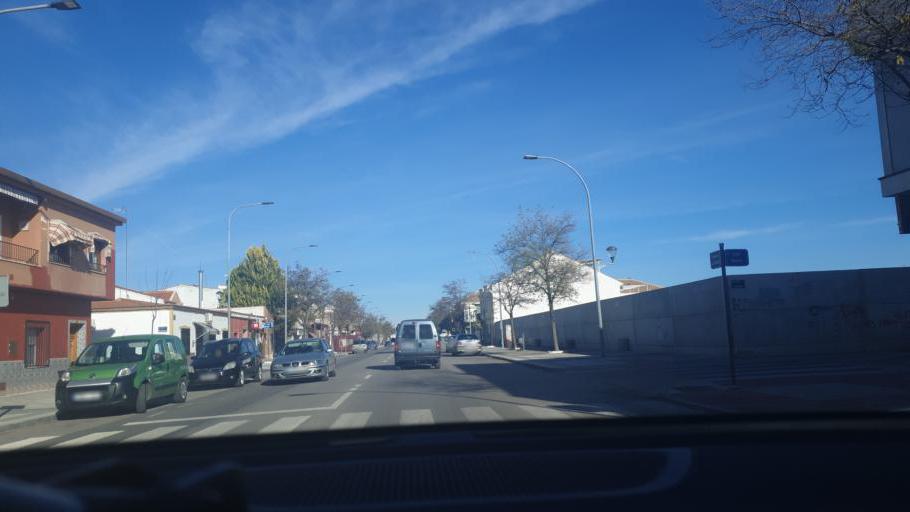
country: ES
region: Castille-La Mancha
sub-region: Provincia de Ciudad Real
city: Tomelloso
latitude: 39.1534
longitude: -3.0104
